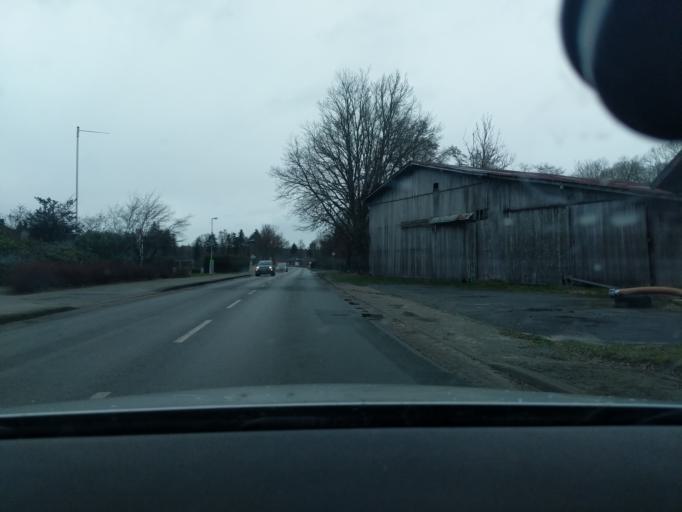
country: DE
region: Lower Saxony
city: Kutenholz
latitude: 53.4851
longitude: 9.3236
